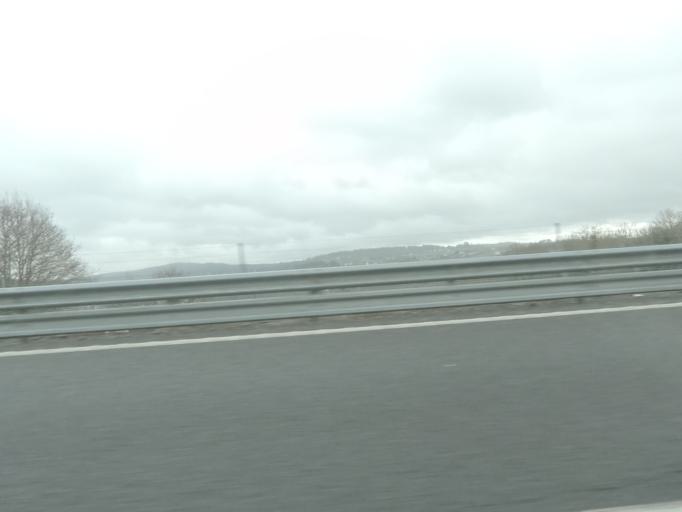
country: ES
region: Galicia
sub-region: Provincia da Coruna
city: Santiago de Compostela
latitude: 42.8422
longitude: -8.5296
